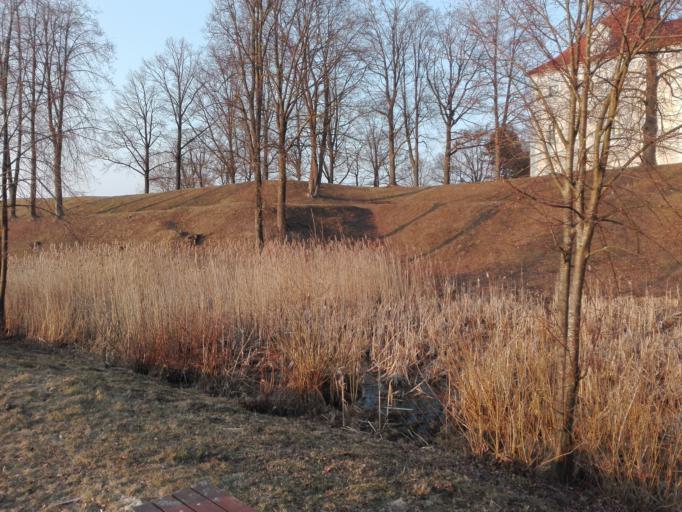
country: LT
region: Panevezys
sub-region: Birzai
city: Birzai
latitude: 56.2045
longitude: 24.7521
